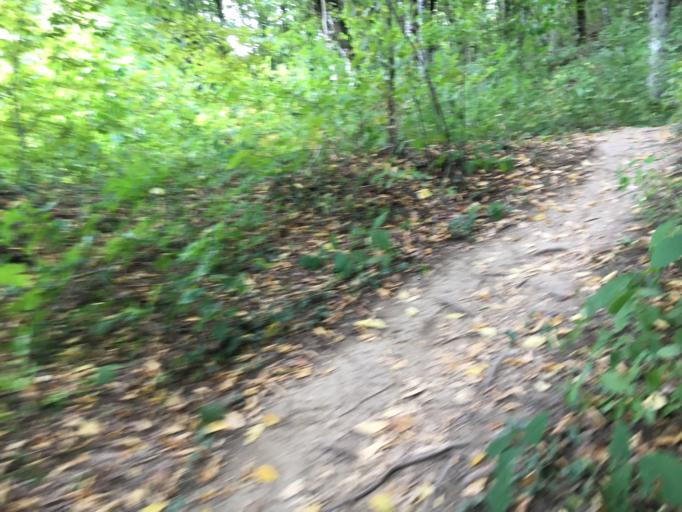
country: RU
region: Krasnodarskiy
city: Tuapse
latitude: 44.2506
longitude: 39.2309
